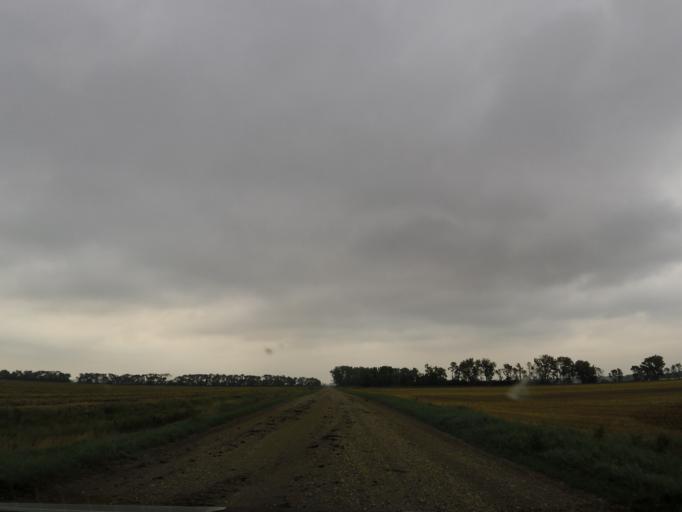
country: US
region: North Dakota
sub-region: Walsh County
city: Grafton
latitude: 48.4997
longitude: -97.1686
